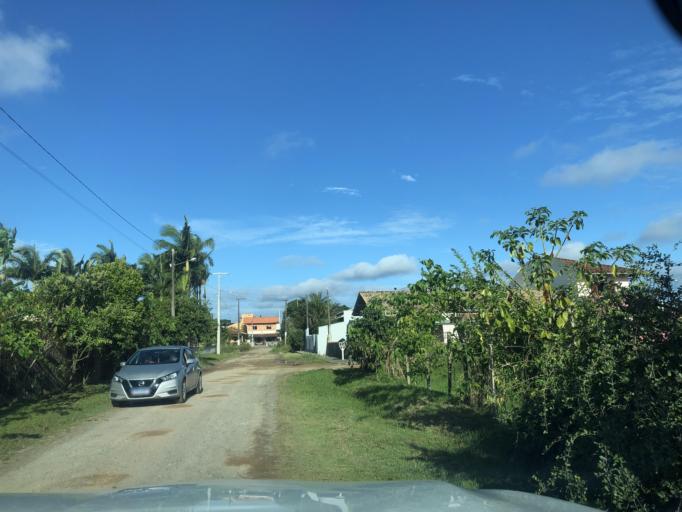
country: BR
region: Santa Catarina
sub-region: Sao Francisco Do Sul
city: Sao Francisco do Sul
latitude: -26.2160
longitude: -48.5284
